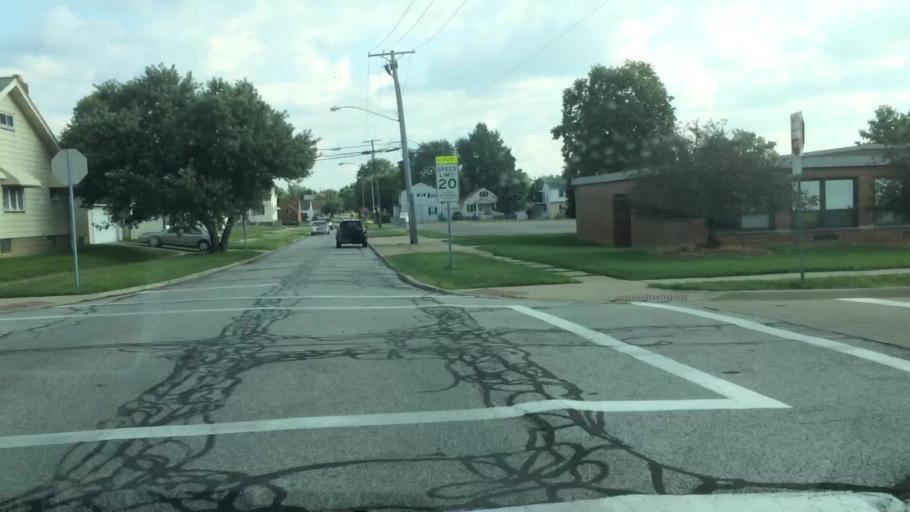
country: US
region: Ohio
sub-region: Cuyahoga County
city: Parma
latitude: 41.4172
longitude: -81.7384
